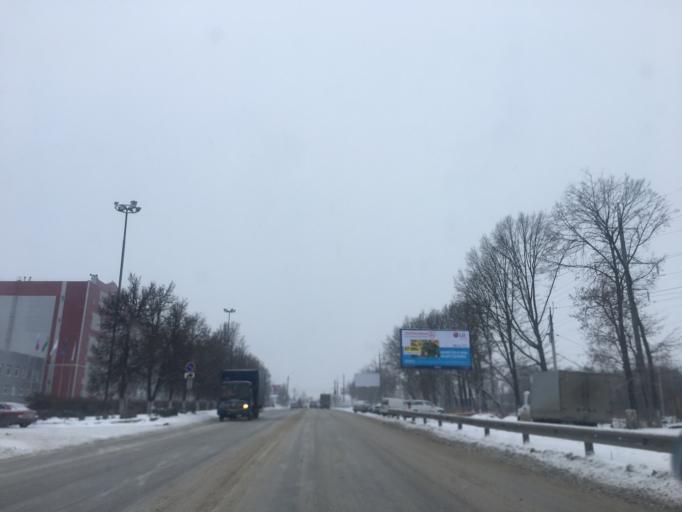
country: RU
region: Tula
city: Kosaya Gora
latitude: 54.1872
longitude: 37.5298
